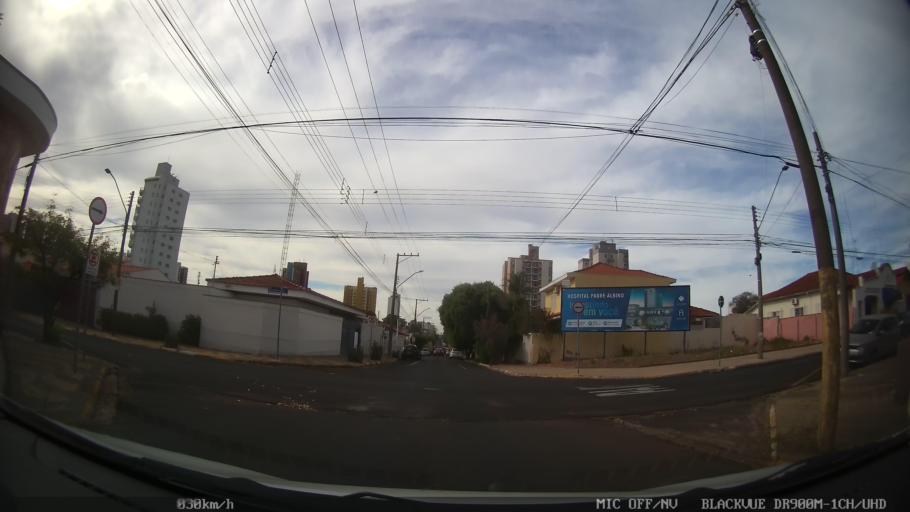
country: BR
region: Sao Paulo
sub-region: Catanduva
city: Catanduva
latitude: -21.1383
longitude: -48.9772
